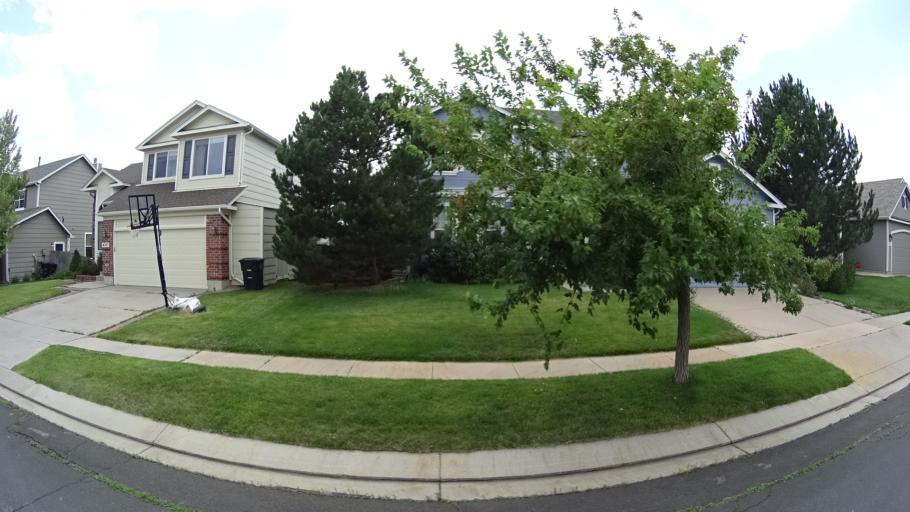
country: US
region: Colorado
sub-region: El Paso County
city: Black Forest
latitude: 38.9616
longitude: -104.7471
